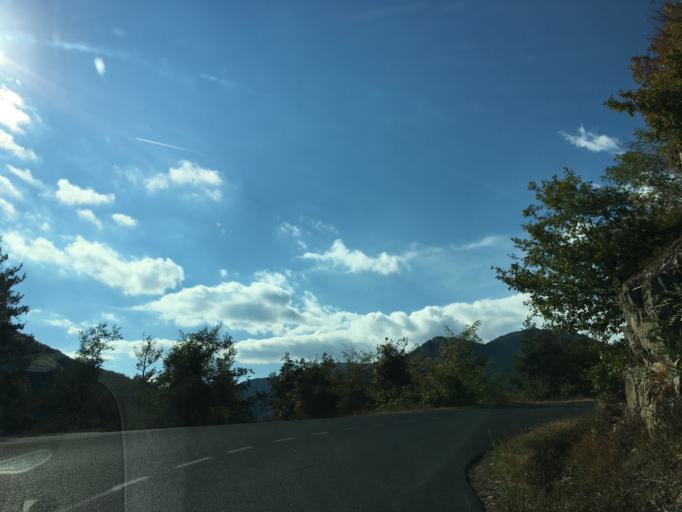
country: BG
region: Smolyan
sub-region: Obshtina Nedelino
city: Nedelino
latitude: 41.4411
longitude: 25.0053
